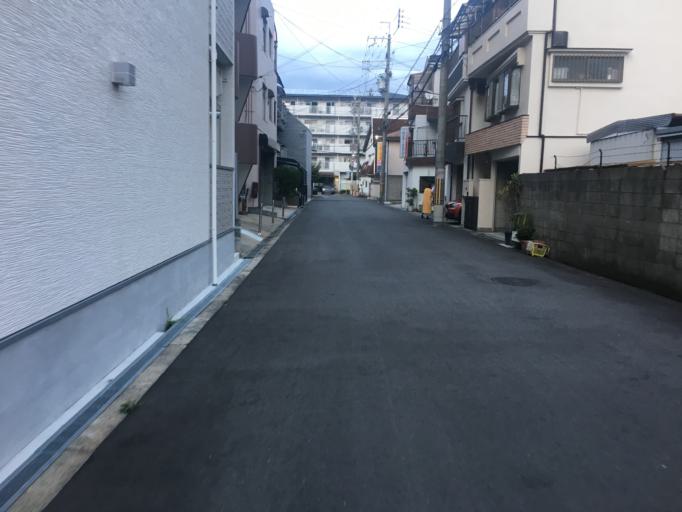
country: JP
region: Osaka
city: Moriguchi
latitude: 34.7479
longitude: 135.5433
